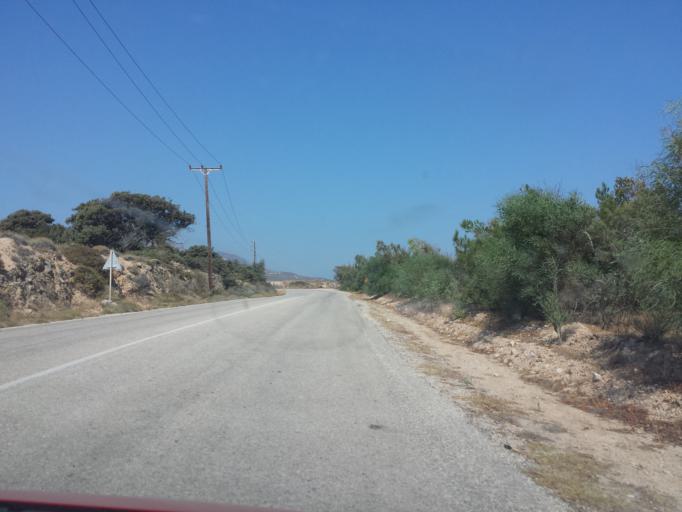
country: GR
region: South Aegean
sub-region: Nomos Kykladon
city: Adamas
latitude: 36.6890
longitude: 24.4523
